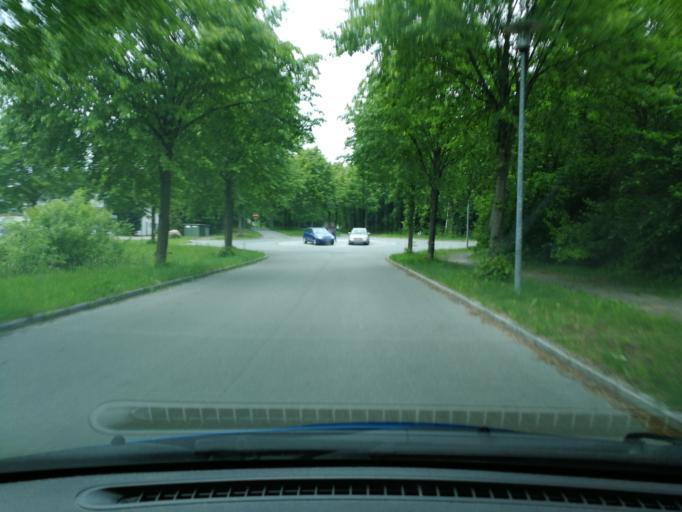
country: DE
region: Schleswig-Holstein
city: Breitenfelde
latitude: 53.6027
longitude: 10.6225
